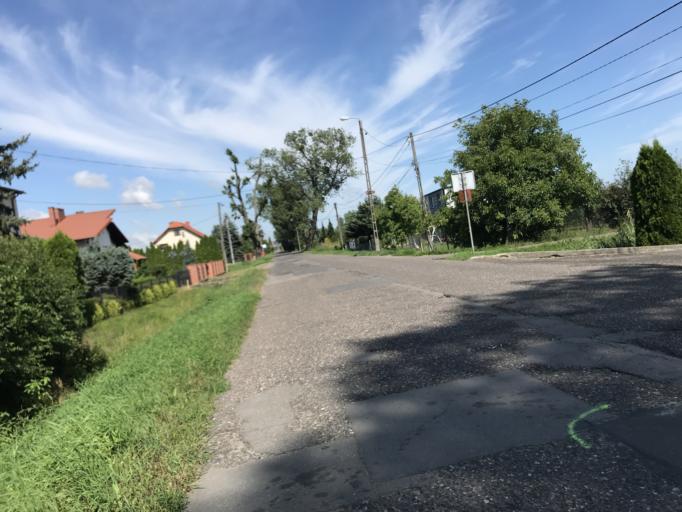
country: PL
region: Pomeranian Voivodeship
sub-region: Gdansk
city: Gdansk
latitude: 54.3255
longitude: 18.6736
